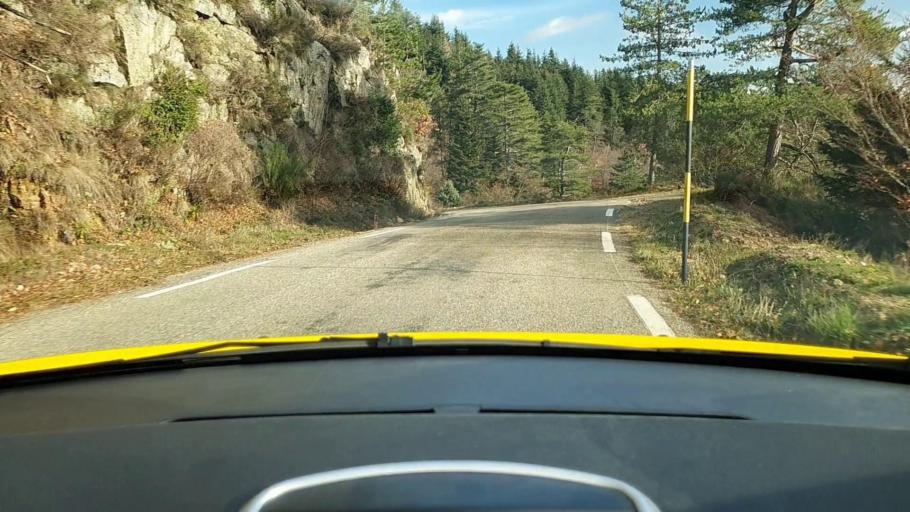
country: FR
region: Languedoc-Roussillon
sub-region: Departement du Gard
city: Branoux-les-Taillades
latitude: 44.3565
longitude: 3.9271
